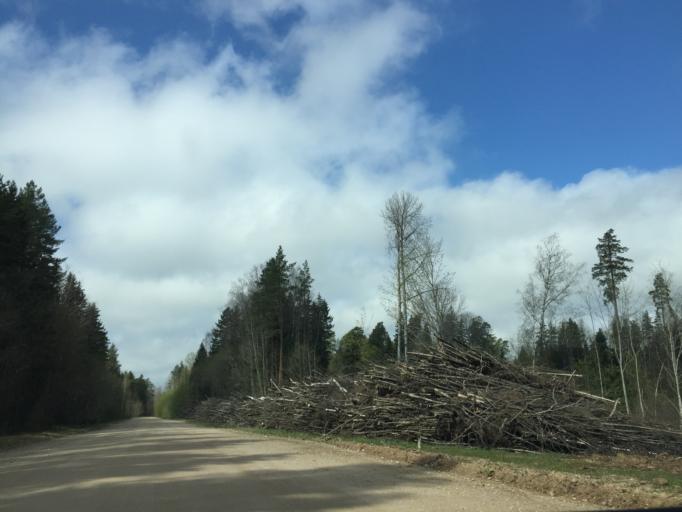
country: LV
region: Apes Novads
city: Ape
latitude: 57.4965
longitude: 26.4111
